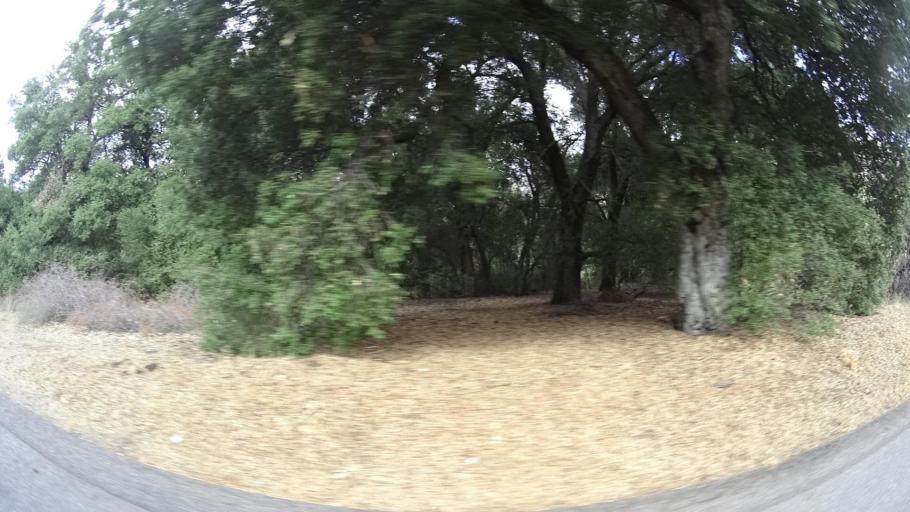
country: US
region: California
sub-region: San Diego County
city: Pine Valley
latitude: 32.8006
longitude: -116.5011
